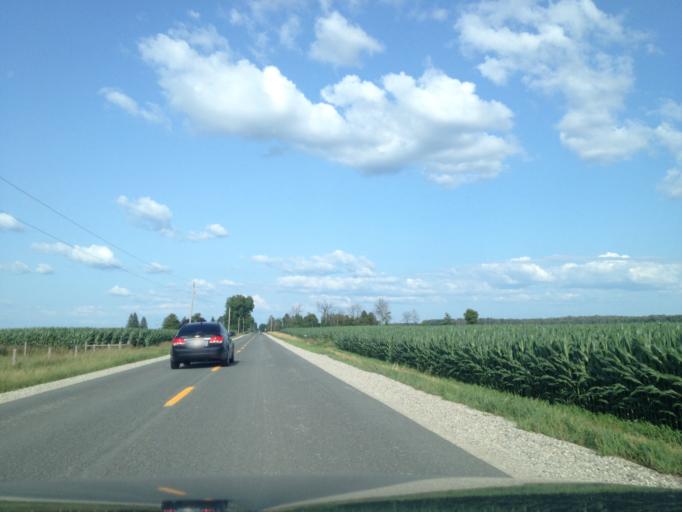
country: CA
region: Ontario
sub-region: Oxford County
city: Woodstock
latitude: 42.9685
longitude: -80.7259
